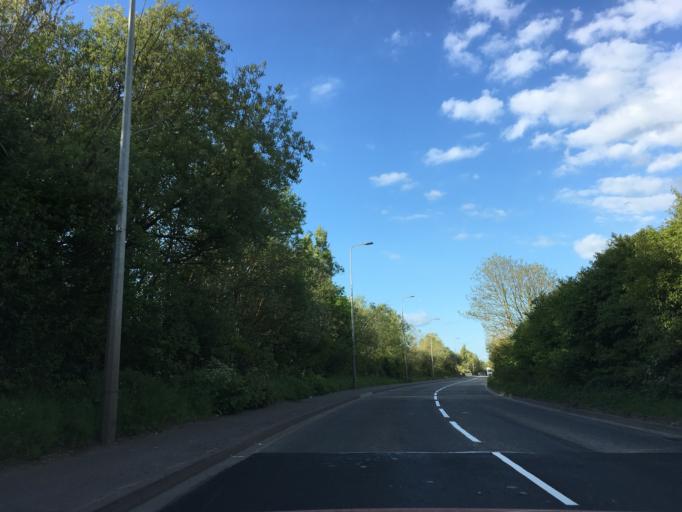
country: GB
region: Wales
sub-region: Cardiff
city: Cardiff
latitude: 51.4943
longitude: -3.1324
